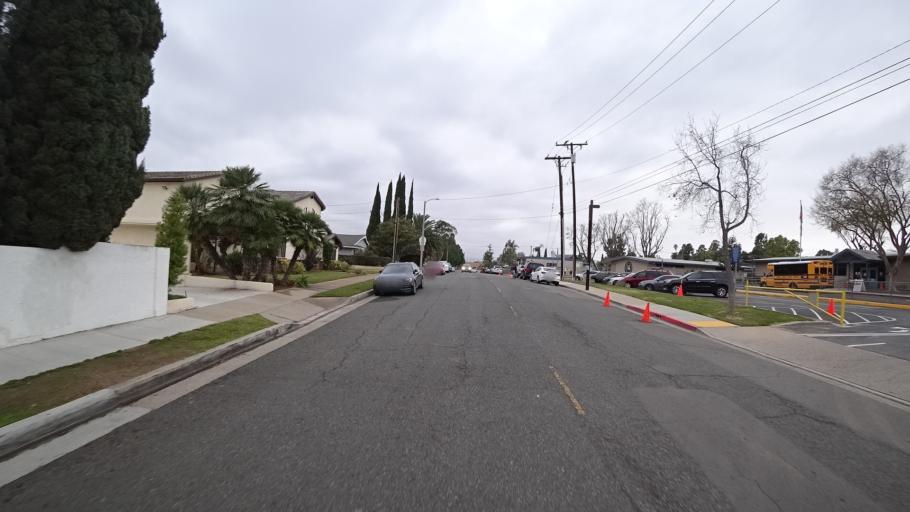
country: US
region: California
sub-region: Orange County
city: North Tustin
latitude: 33.7788
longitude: -117.8074
